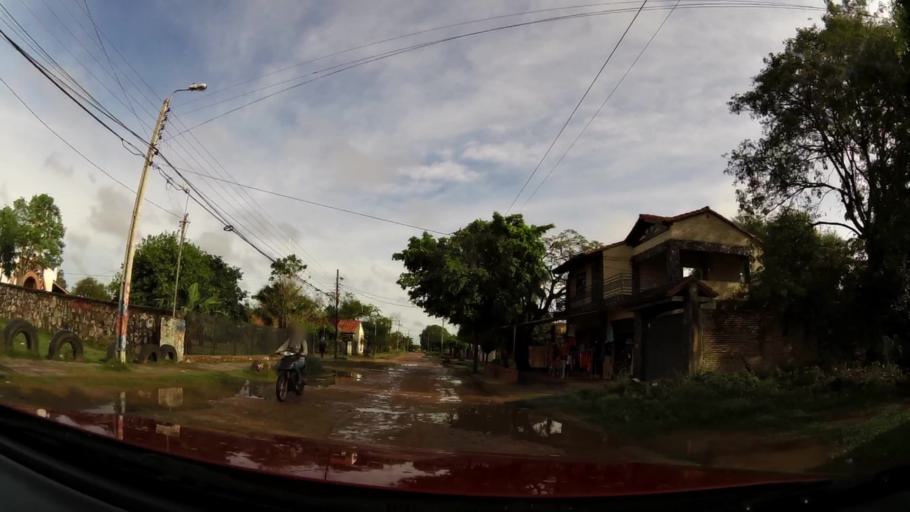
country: PY
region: Central
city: Limpio
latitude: -25.1871
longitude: -57.4866
